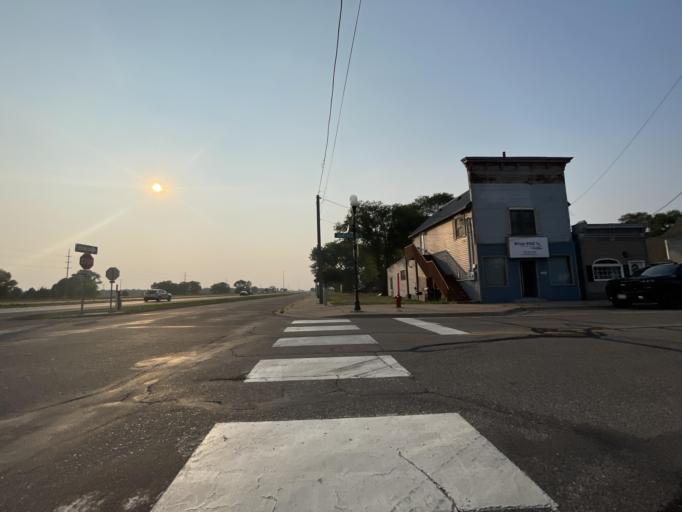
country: US
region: Minnesota
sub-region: Sherburne County
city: Becker
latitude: 45.3932
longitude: -93.8770
